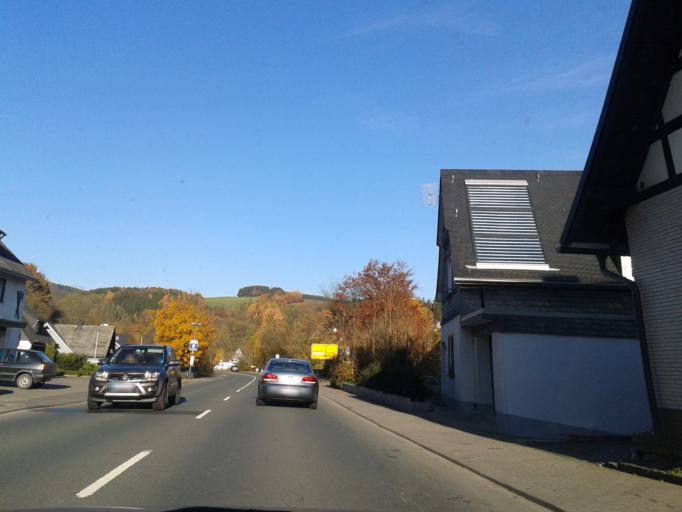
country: DE
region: North Rhine-Westphalia
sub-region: Regierungsbezirk Arnsberg
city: Olsberg
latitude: 51.3056
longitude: 8.5007
